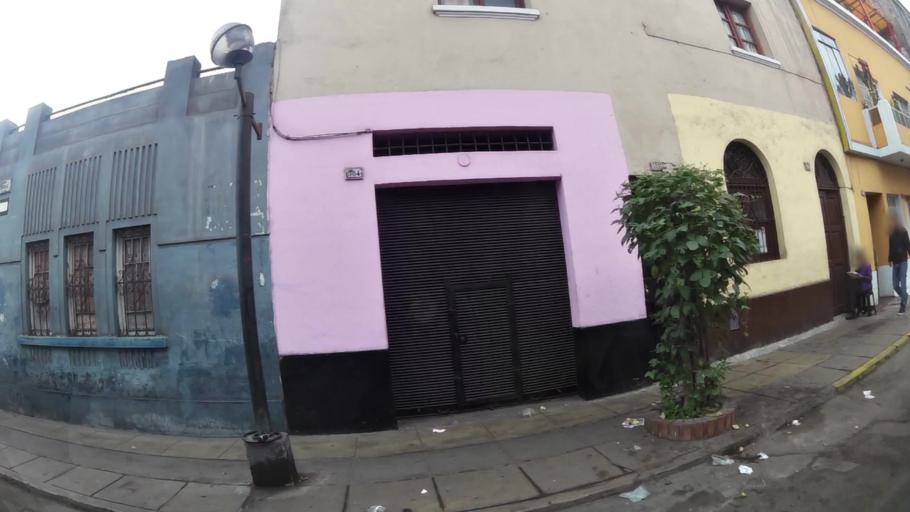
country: PE
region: Lima
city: Lima
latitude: -12.0540
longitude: -77.0513
